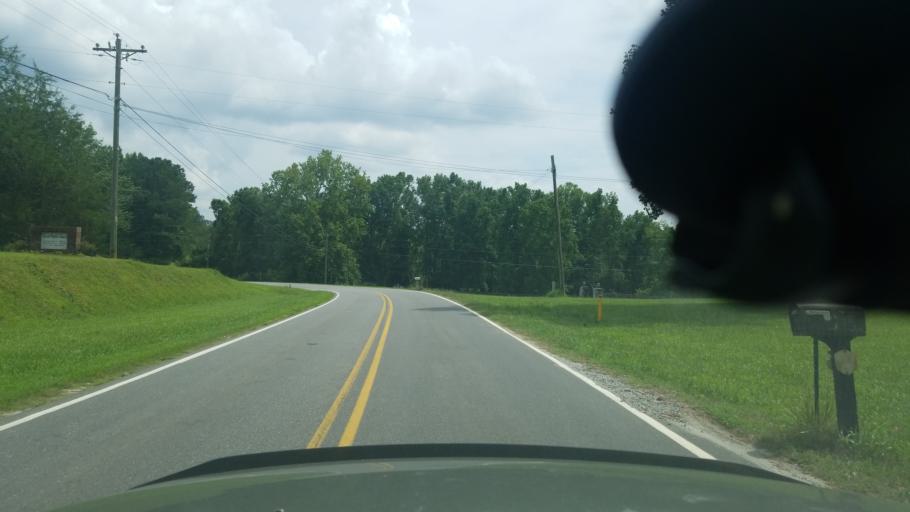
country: US
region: Georgia
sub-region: Dawson County
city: Dawsonville
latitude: 34.3249
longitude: -84.1715
